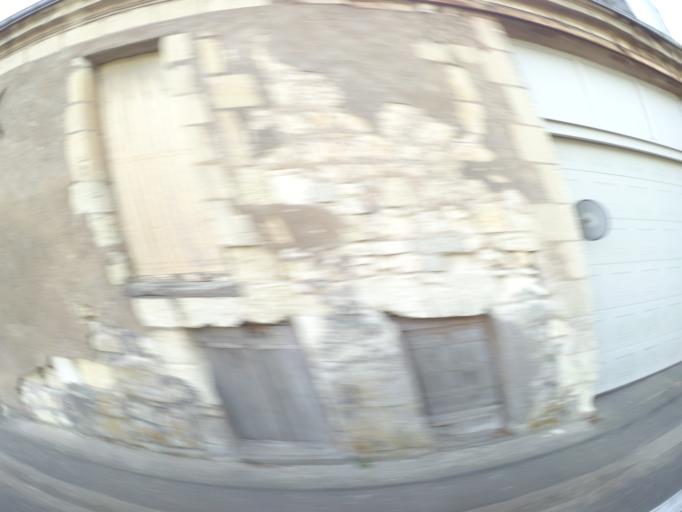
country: FR
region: Centre
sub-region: Departement d'Indre-et-Loire
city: La Chapelle-sur-Loire
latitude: 47.2392
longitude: 0.1908
